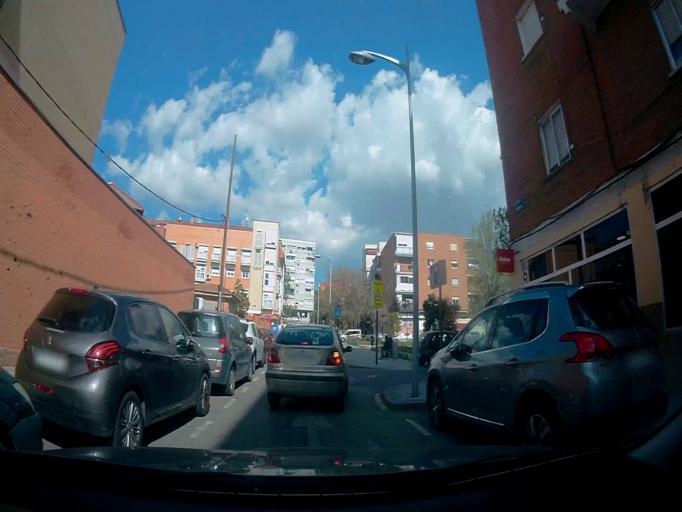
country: ES
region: Madrid
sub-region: Provincia de Madrid
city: Alcorcon
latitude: 40.3489
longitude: -3.8307
